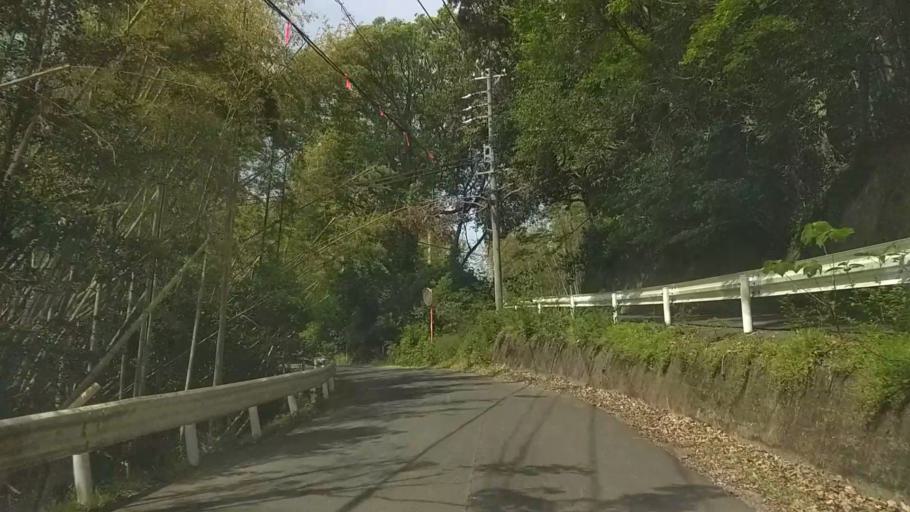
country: JP
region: Shizuoka
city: Kosai-shi
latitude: 34.7715
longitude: 137.6282
